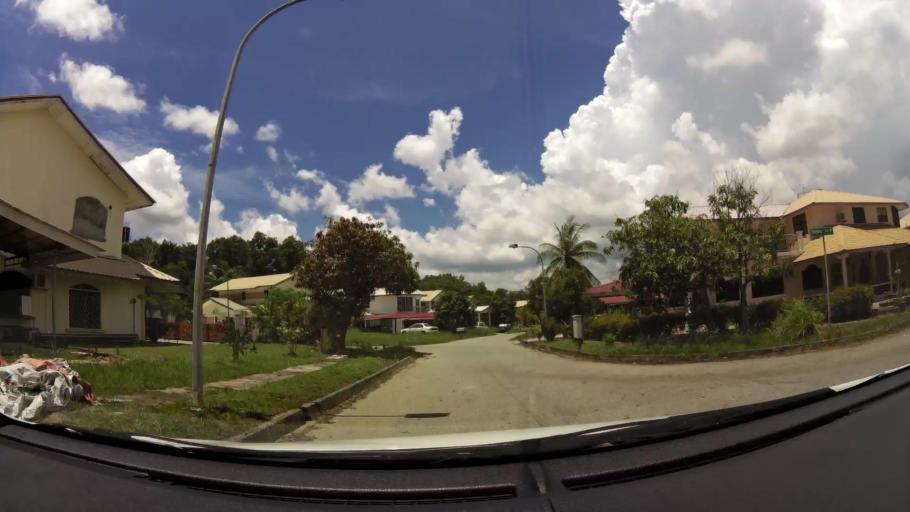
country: BN
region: Brunei and Muara
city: Bandar Seri Begawan
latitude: 4.9636
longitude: 114.9174
